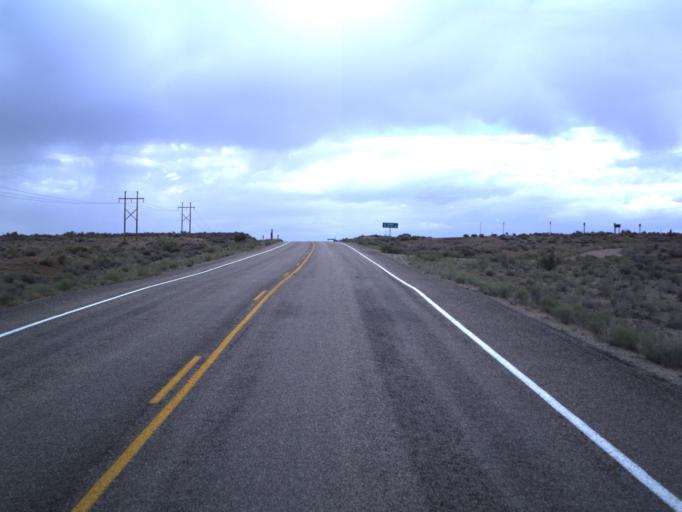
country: US
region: Colorado
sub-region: Rio Blanco County
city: Rangely
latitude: 40.0756
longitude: -109.2078
